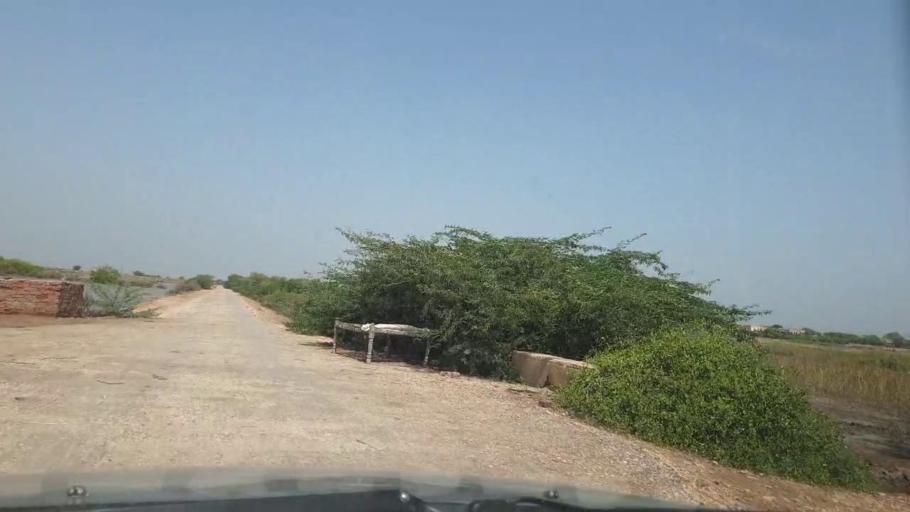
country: PK
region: Sindh
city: Tando Ghulam Ali
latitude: 25.0993
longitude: 68.8021
